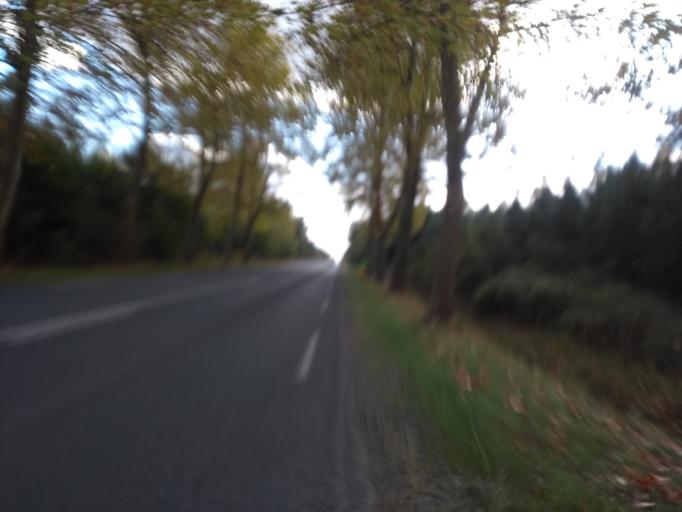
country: FR
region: Aquitaine
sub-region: Departement de la Gironde
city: Saint-Aubin-de-Medoc
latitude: 44.6798
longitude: -0.7257
